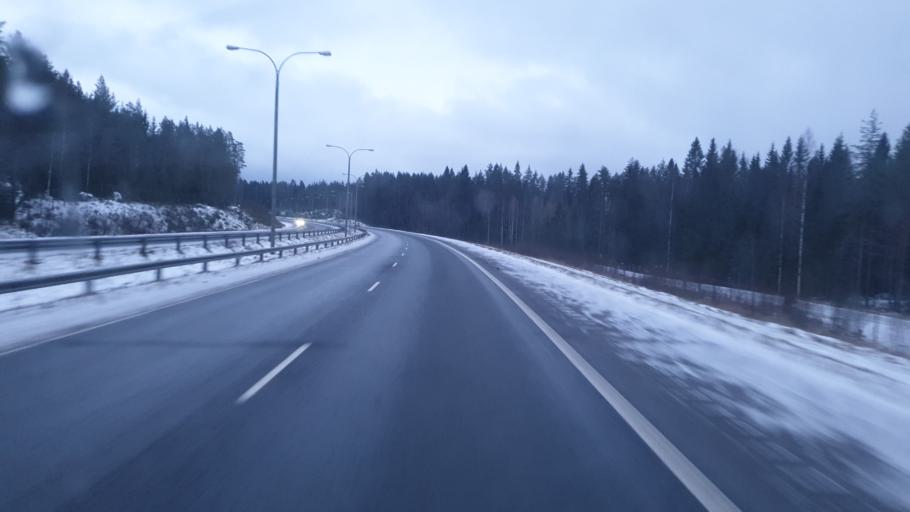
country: FI
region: Northern Savo
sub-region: Kuopio
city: Siilinjaervi
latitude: 63.0053
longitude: 27.6808
